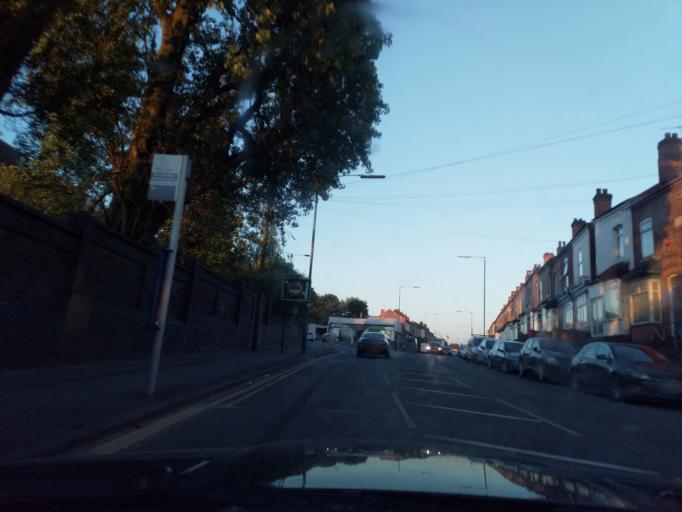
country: GB
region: England
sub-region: City and Borough of Birmingham
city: Acocks Green
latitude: 52.4533
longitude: -1.8417
